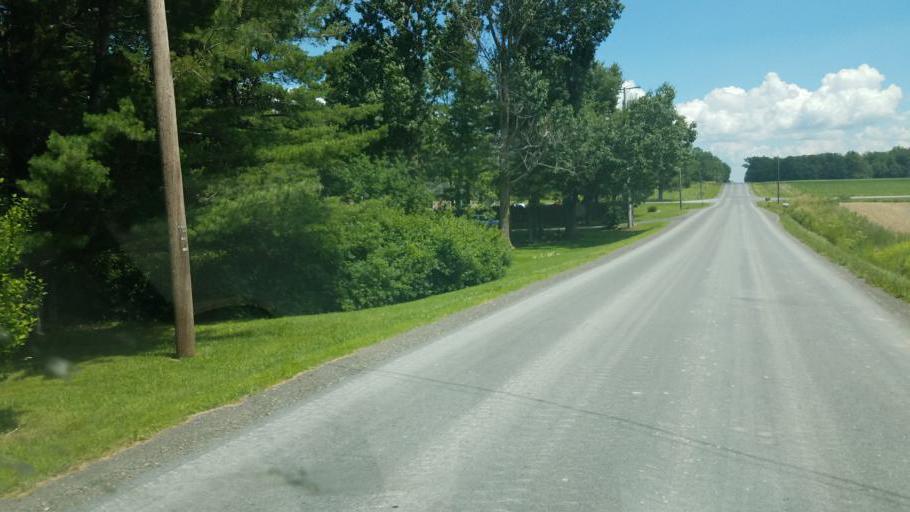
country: US
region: New York
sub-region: Yates County
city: Keuka Park
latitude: 42.5931
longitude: -77.0281
